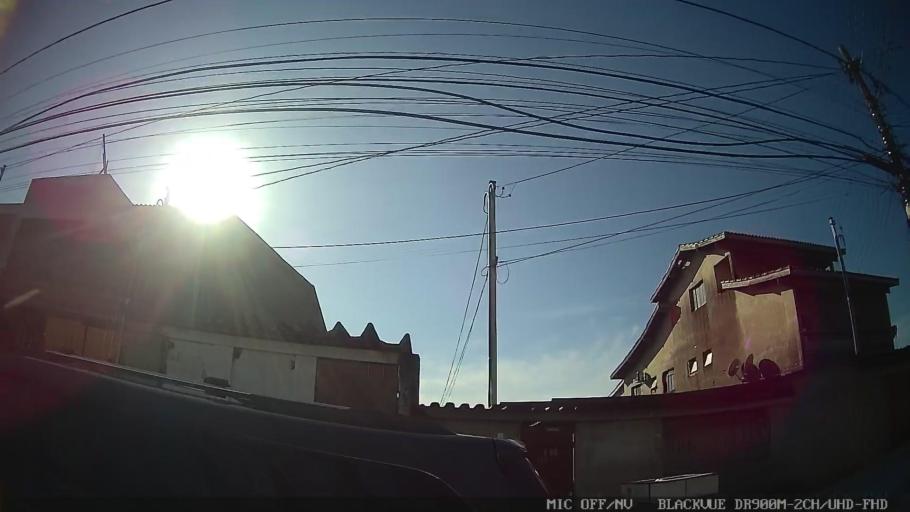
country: BR
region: Sao Paulo
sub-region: Guaruja
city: Guaruja
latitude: -23.9608
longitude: -46.2832
